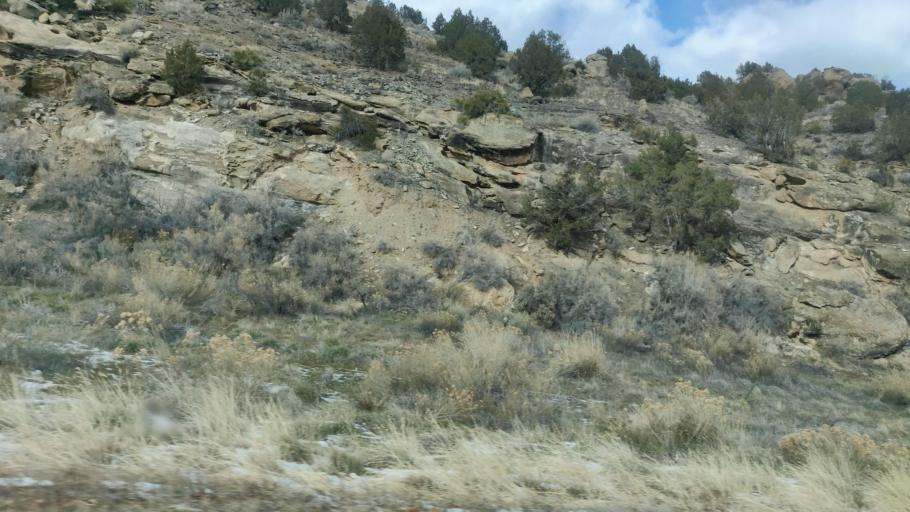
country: US
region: Colorado
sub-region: Mesa County
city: Palisade
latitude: 39.1916
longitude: -108.2440
